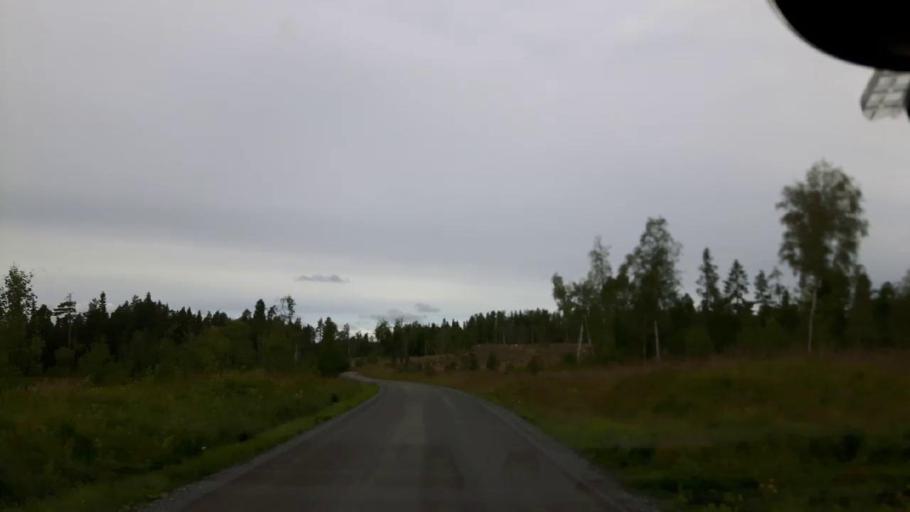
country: SE
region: Jaemtland
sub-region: Krokoms Kommun
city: Krokom
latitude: 63.2780
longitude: 14.3938
